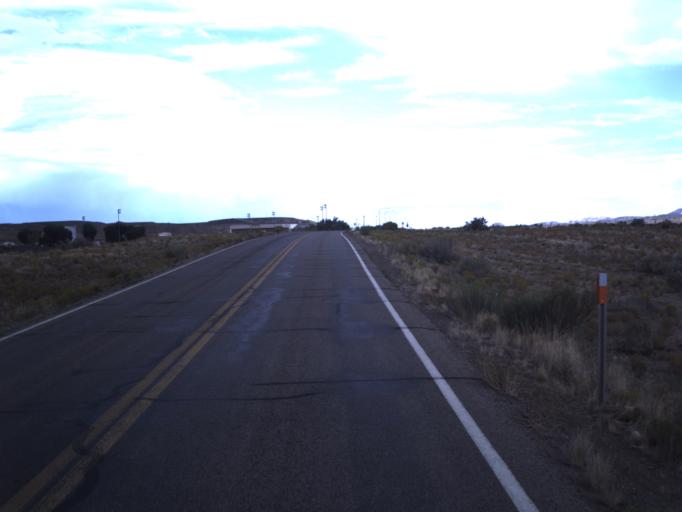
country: US
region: Utah
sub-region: San Juan County
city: Blanding
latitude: 37.2687
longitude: -109.3191
